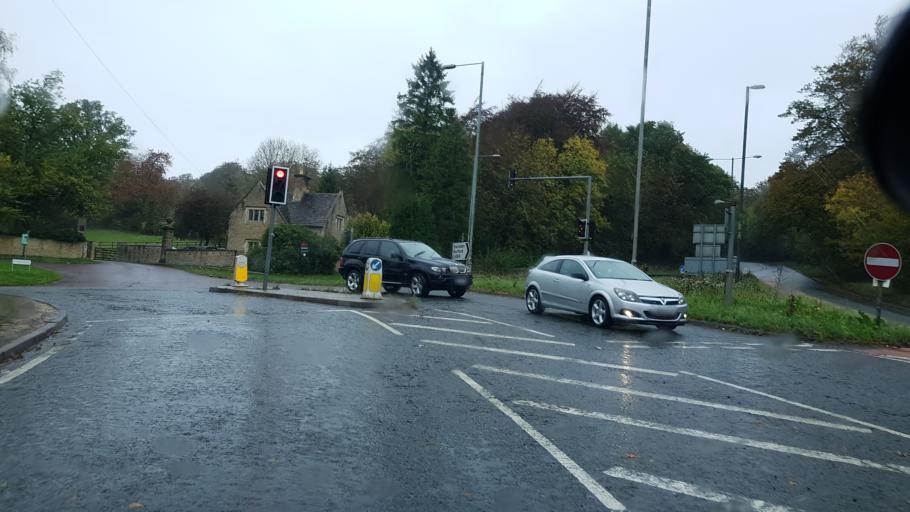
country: GB
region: England
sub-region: Gloucestershire
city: Stow on the Wold
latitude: 51.9175
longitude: -1.7250
